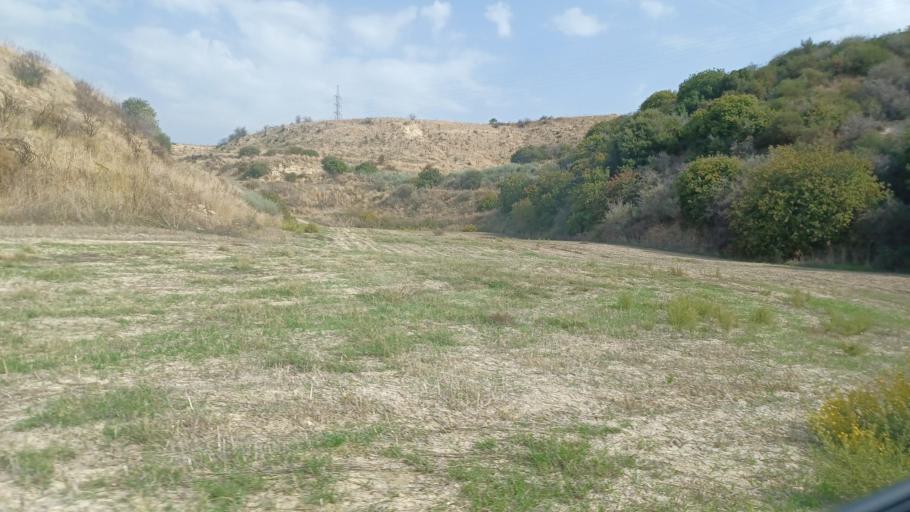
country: CY
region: Pafos
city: Polis
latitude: 34.9713
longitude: 32.4580
